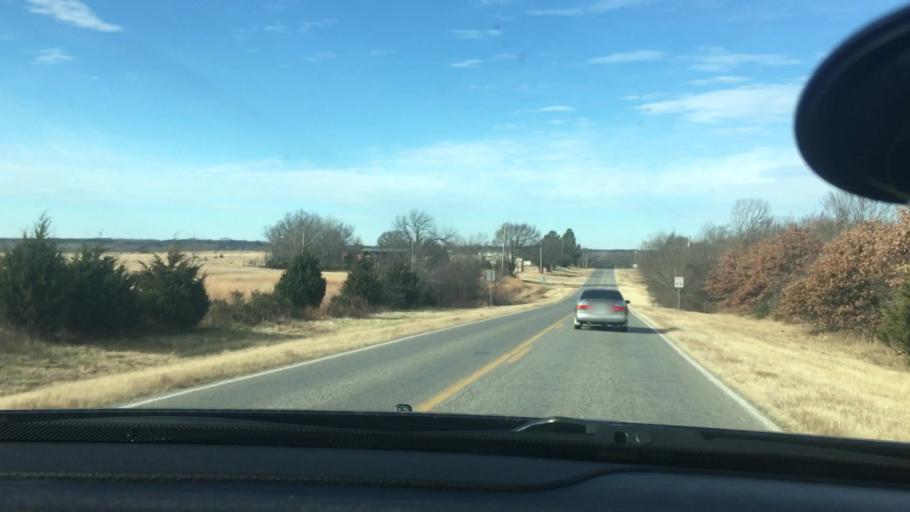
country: US
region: Oklahoma
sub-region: Seminole County
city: Konawa
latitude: 34.9493
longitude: -96.7425
